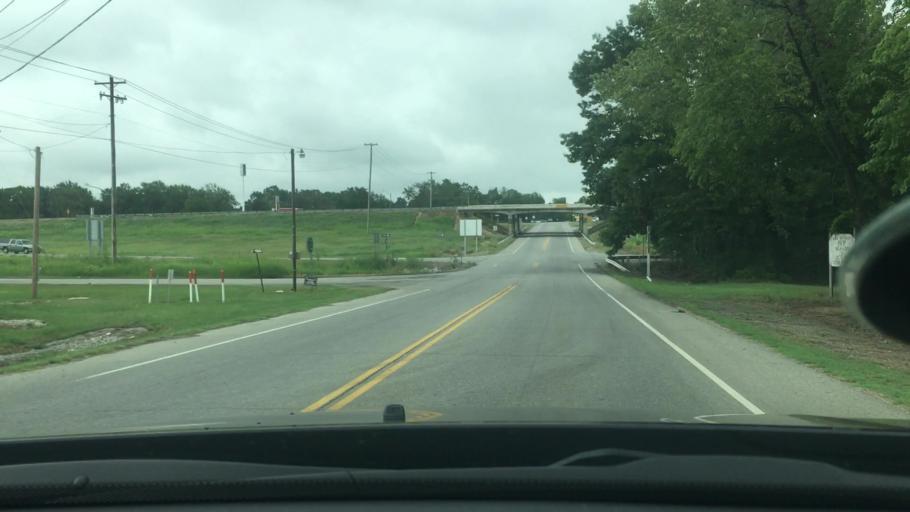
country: US
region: Oklahoma
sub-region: Bryan County
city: Colbert
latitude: 33.8530
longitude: -96.5139
